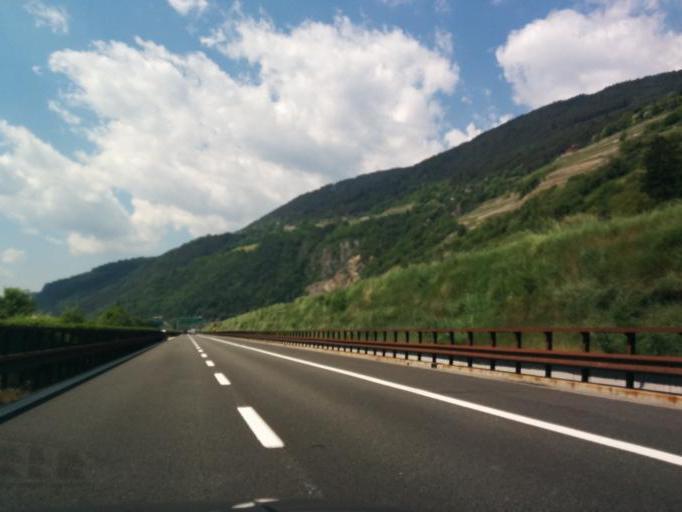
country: IT
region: Trentino-Alto Adige
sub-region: Bolzano
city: Bressanone
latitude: 46.6888
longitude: 11.6356
